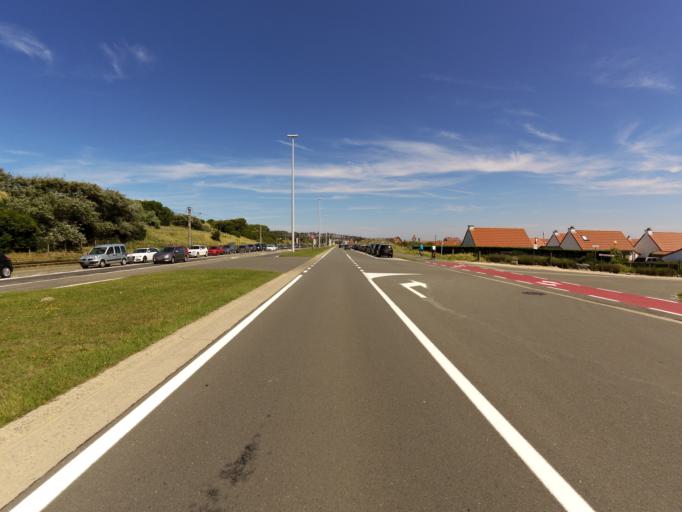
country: BE
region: Flanders
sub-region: Provincie West-Vlaanderen
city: Wenduine
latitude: 51.3071
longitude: 3.0985
